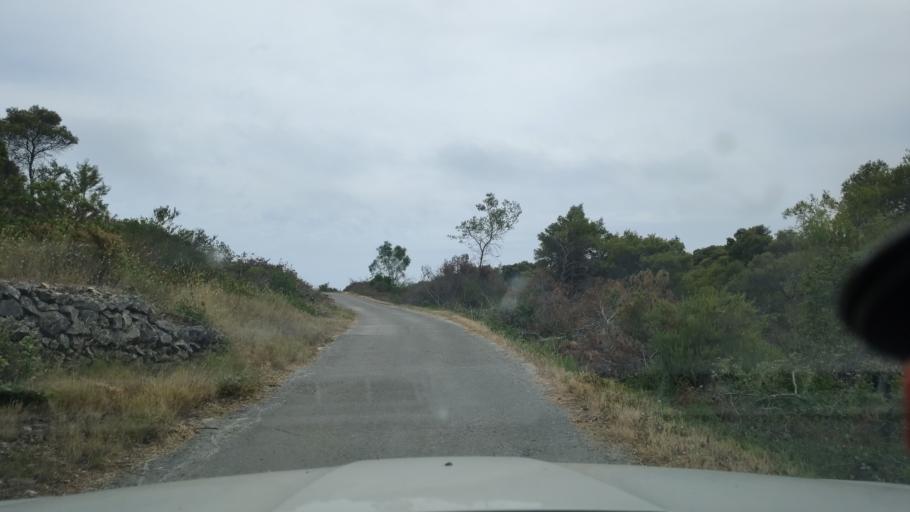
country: HR
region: Splitsko-Dalmatinska
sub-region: Grad Vis
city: Vis
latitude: 43.0291
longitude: 16.1678
